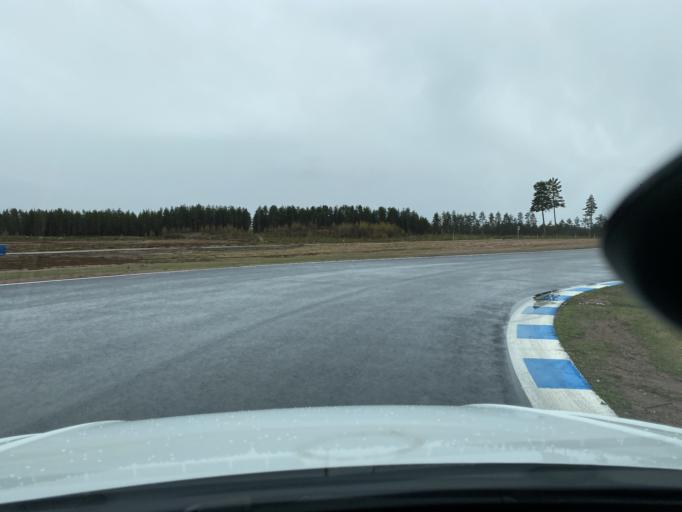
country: FI
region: Satakunta
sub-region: Pori
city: Vampula
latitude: 60.9759
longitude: 22.6628
